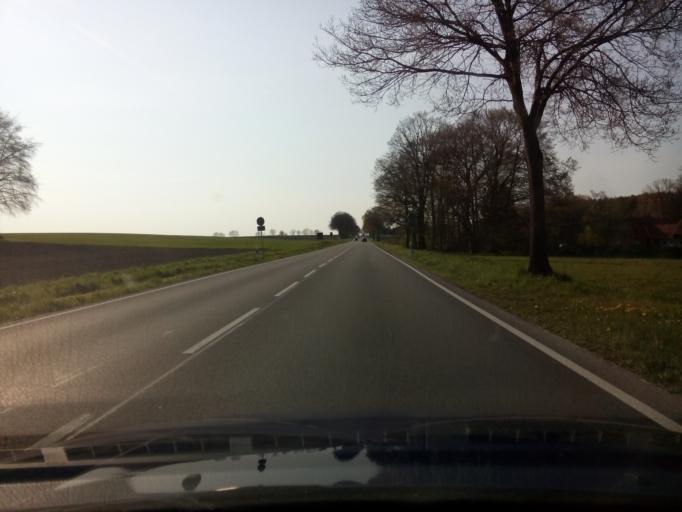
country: DE
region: Lower Saxony
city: Sustedt
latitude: 52.8347
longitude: 8.9168
